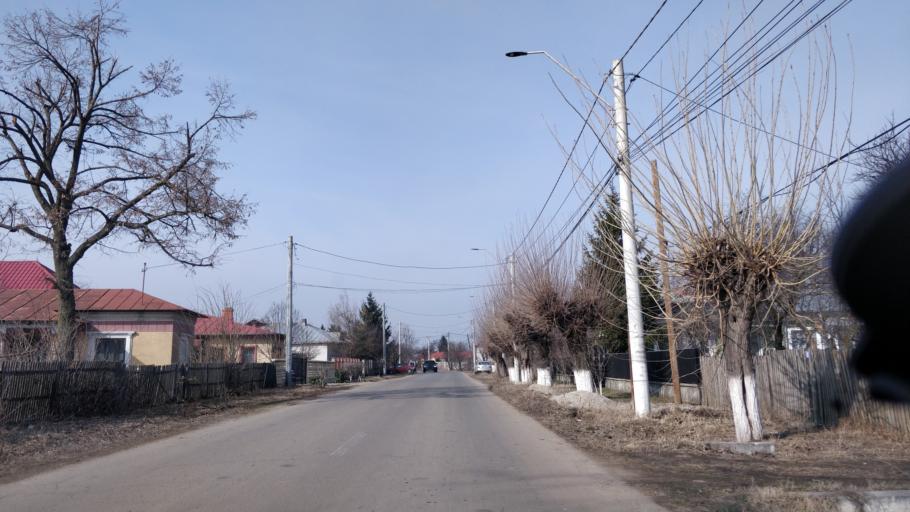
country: RO
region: Giurgiu
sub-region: Comuna Ulmi
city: Ulmi
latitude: 44.4629
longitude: 25.7775
